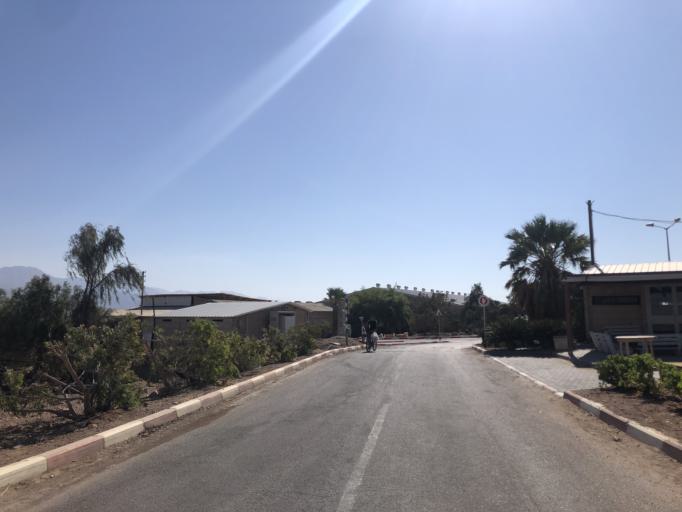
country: IL
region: Southern District
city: Eilat
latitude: 29.5820
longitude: 34.9642
